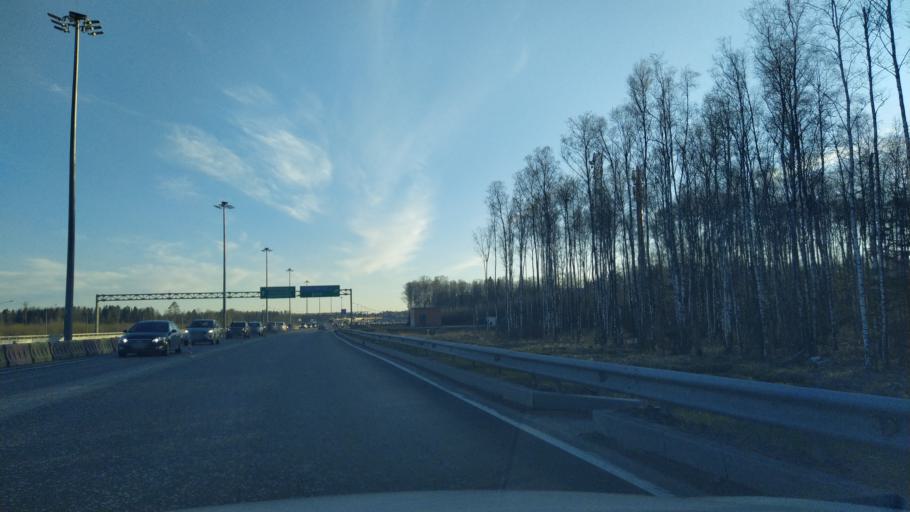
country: RU
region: St.-Petersburg
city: Levashovo
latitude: 60.0649
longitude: 30.1652
